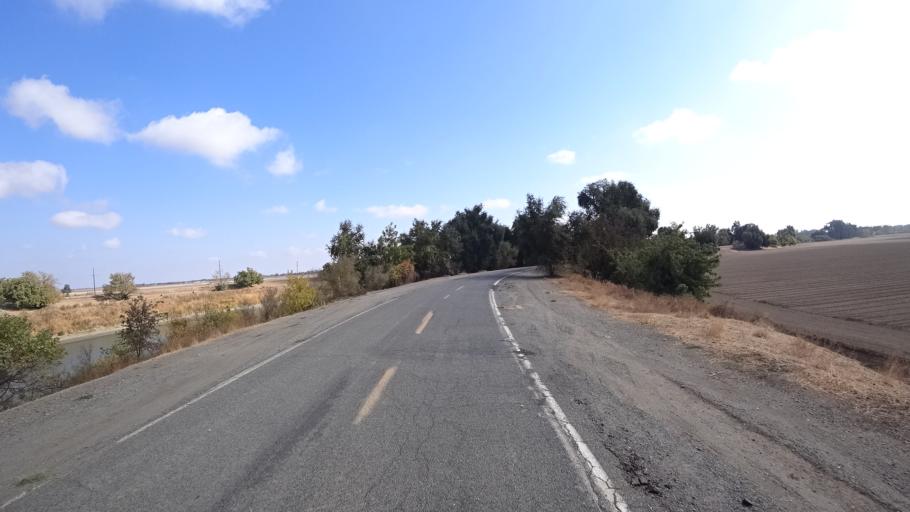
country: US
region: California
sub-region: Yolo County
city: Woodland
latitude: 38.7632
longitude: -121.6832
